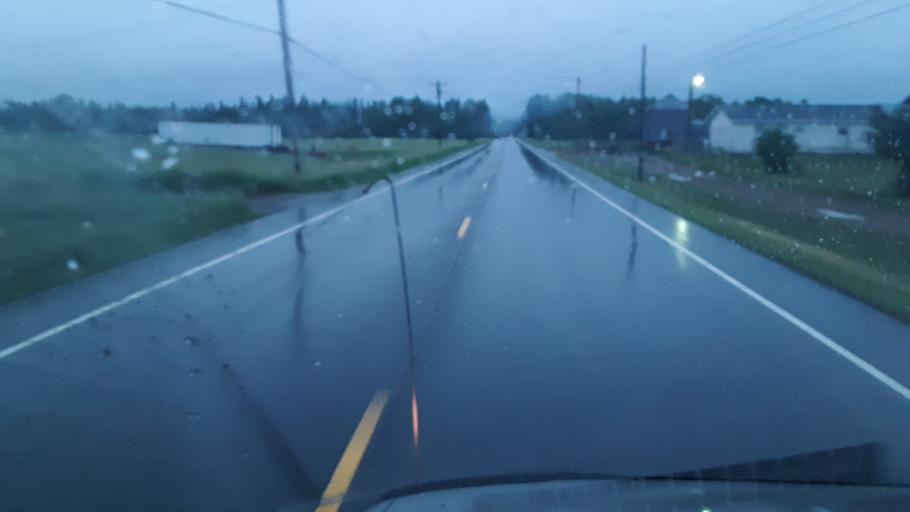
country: US
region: Maine
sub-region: Penobscot County
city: Patten
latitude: 45.9515
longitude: -68.4525
